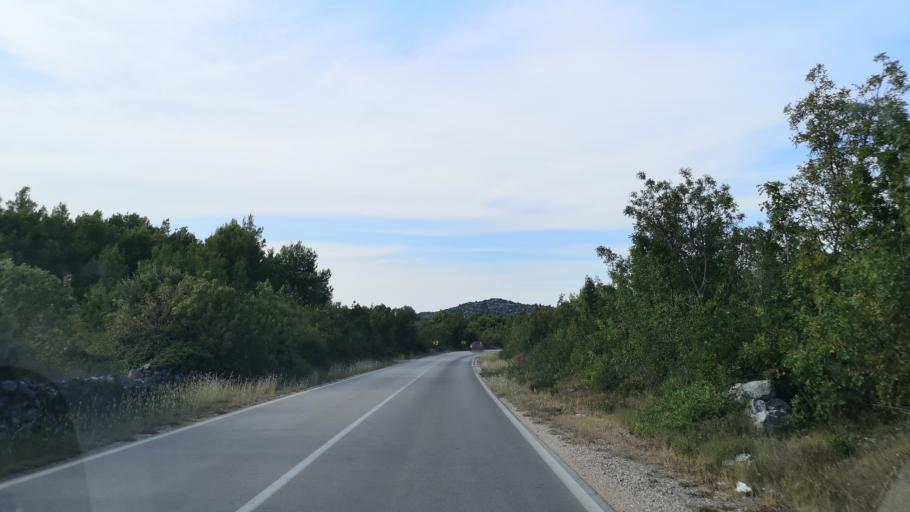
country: HR
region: Sibensko-Kniniska
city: Vodice
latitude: 43.7926
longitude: 15.7710
